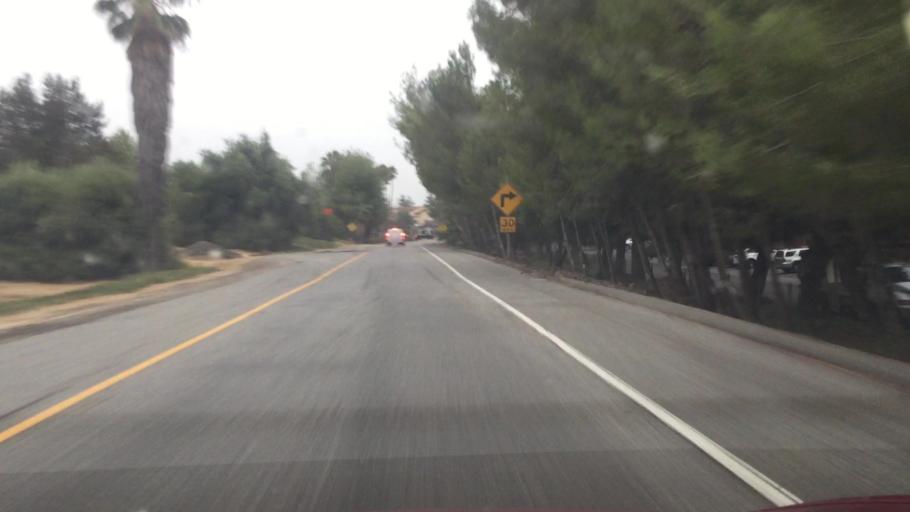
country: US
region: California
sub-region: Santa Clara County
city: Milpitas
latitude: 37.4362
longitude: -121.8900
